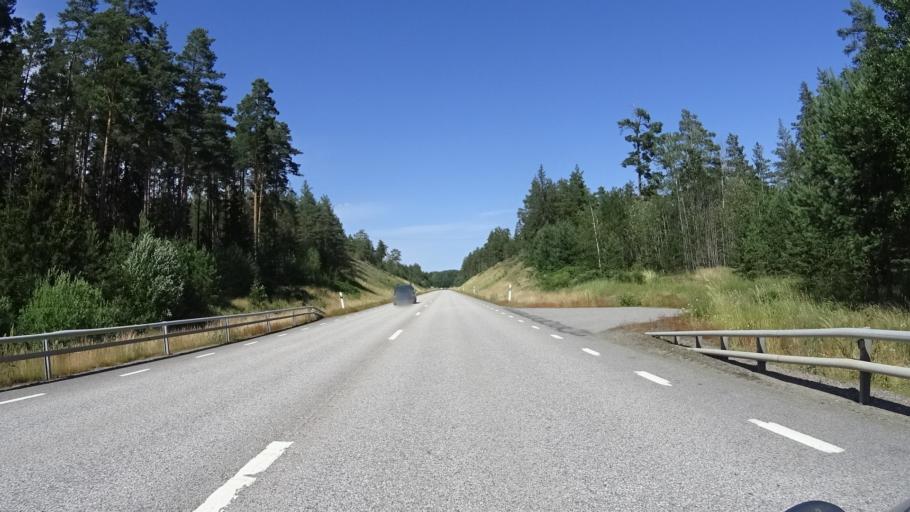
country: SE
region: Kalmar
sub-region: Vasterviks Kommun
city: Gamleby
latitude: 57.9302
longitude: 16.3777
